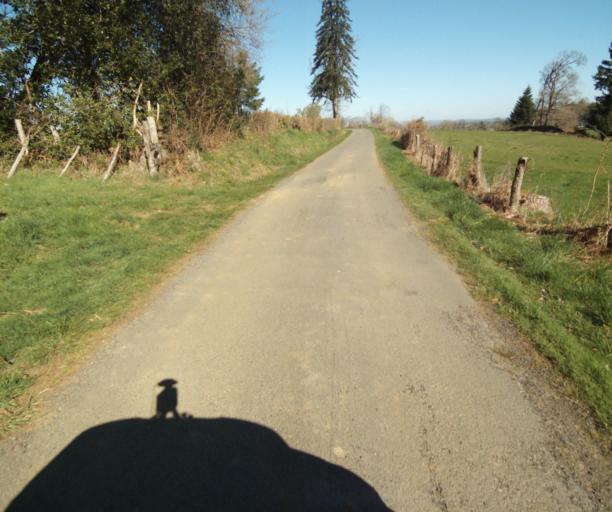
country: FR
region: Limousin
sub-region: Departement de la Correze
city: Chamboulive
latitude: 45.4115
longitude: 1.6909
